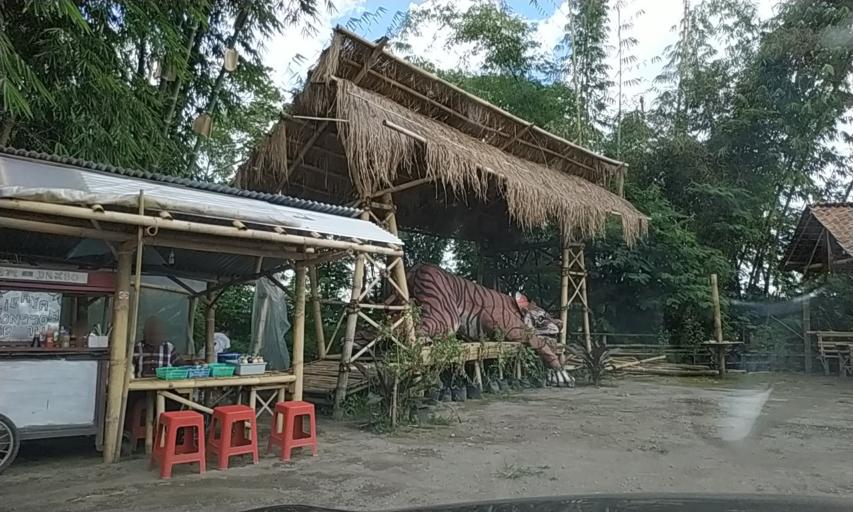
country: ID
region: Central Java
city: Muntilan
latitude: -7.5379
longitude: 110.3567
